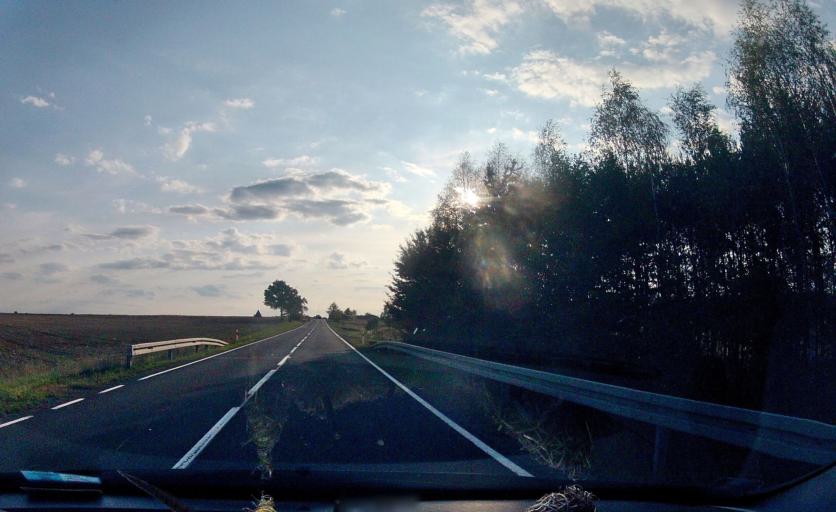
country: PL
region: Opole Voivodeship
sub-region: Powiat oleski
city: Gorzow Slaski
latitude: 51.0051
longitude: 18.3466
